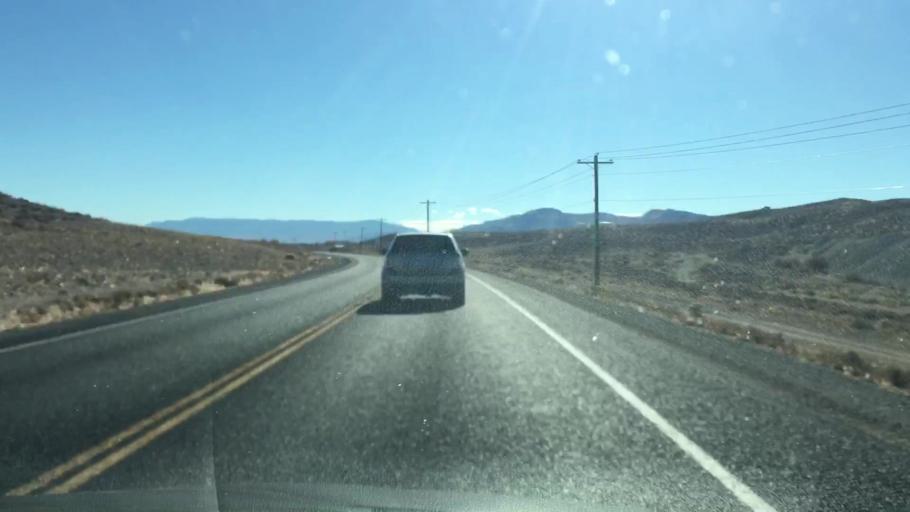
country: US
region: Nevada
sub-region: Lyon County
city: Yerington
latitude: 39.0112
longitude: -119.1829
